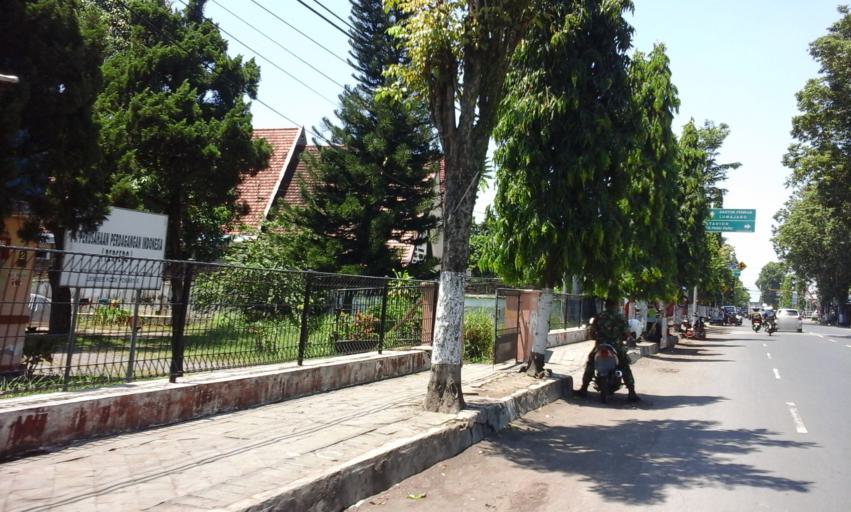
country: ID
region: East Java
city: Krajan
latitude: -8.1602
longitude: 113.7090
